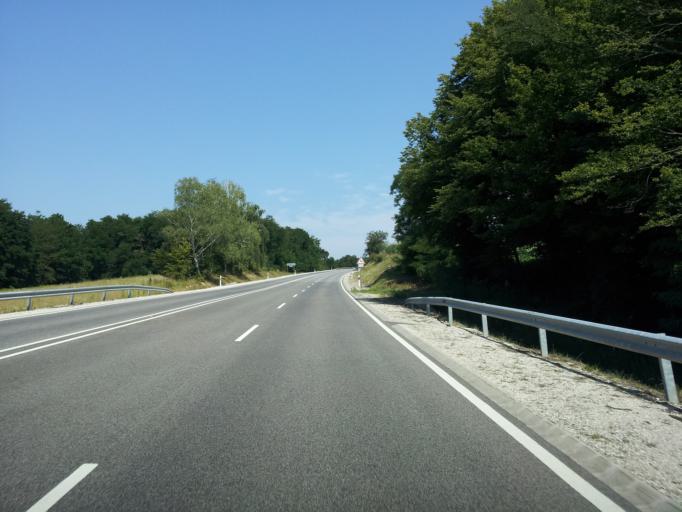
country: HU
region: Zala
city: Pacsa
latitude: 46.8153
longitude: 17.0563
